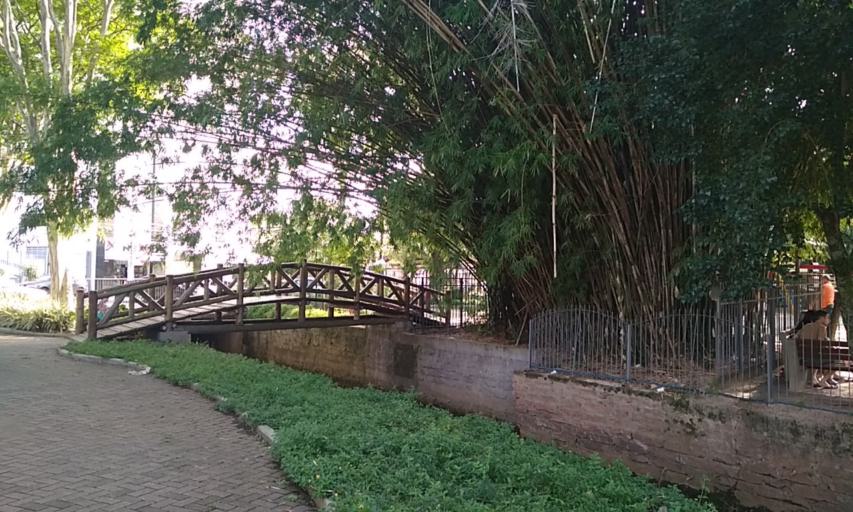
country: BR
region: Rio Grande do Sul
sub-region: Igrejinha
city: Igrejinha
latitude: -29.5731
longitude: -50.7917
